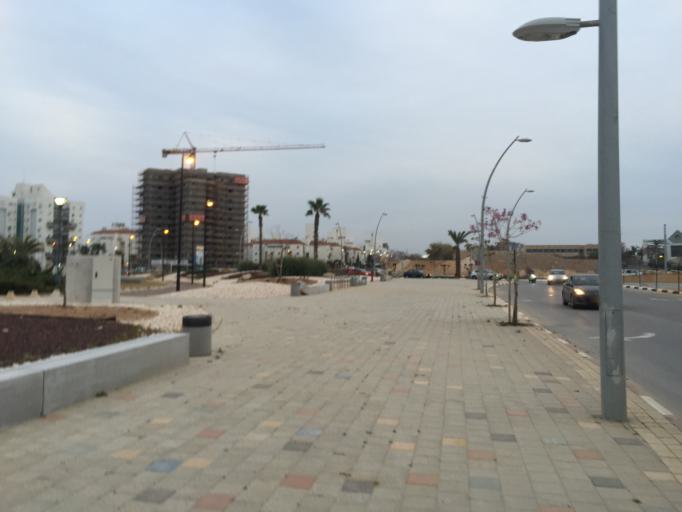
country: IL
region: Haifa
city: Qesarya
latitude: 32.5041
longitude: 34.9199
